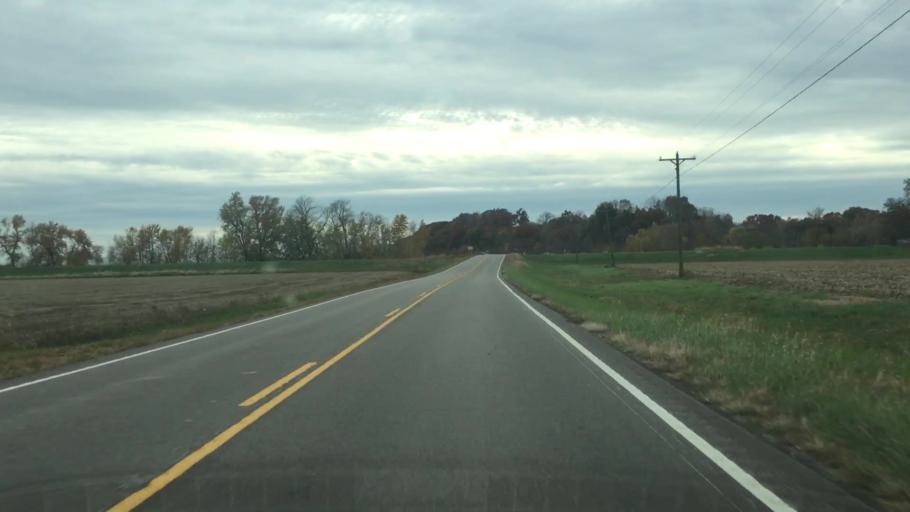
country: US
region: Missouri
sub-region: Callaway County
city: Fulton
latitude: 38.6983
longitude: -91.8243
